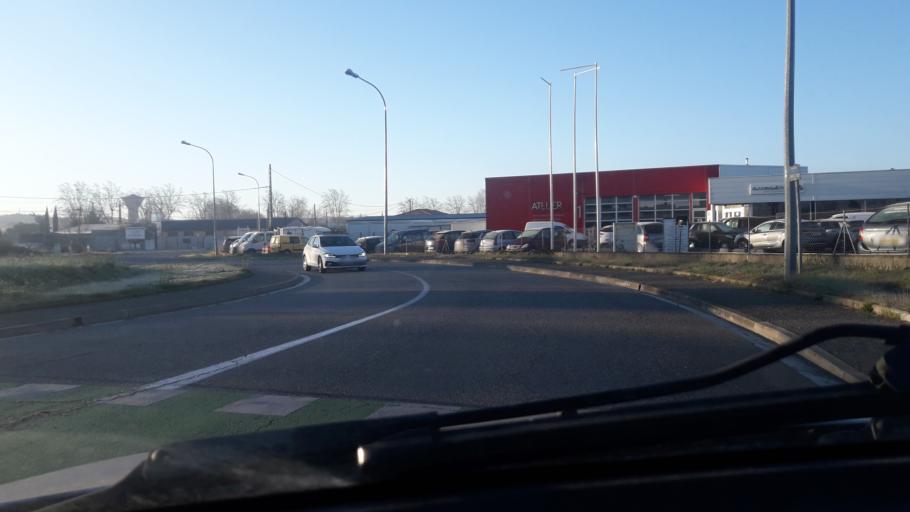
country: FR
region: Midi-Pyrenees
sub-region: Departement de la Haute-Garonne
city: Carbonne
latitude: 43.3098
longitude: 1.2224
